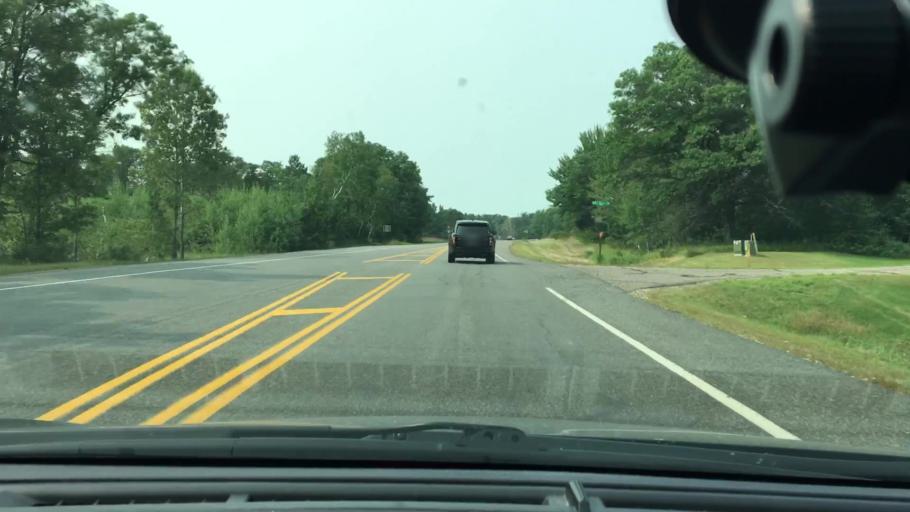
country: US
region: Minnesota
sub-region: Crow Wing County
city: Breezy Point
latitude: 46.4856
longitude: -94.1600
